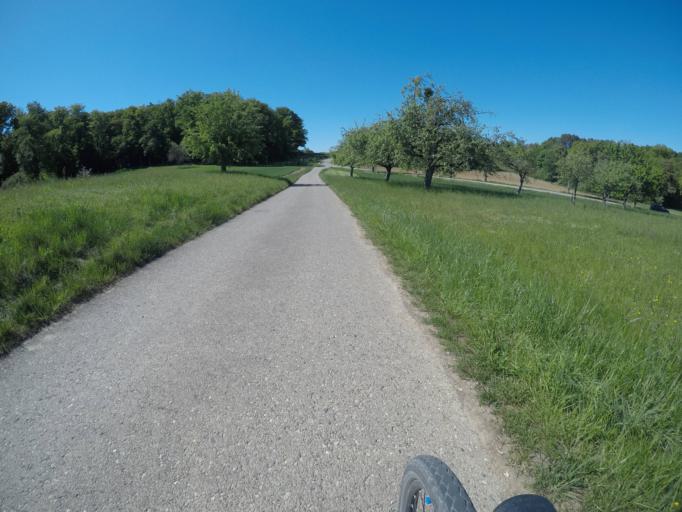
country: DE
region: Baden-Wuerttemberg
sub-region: Regierungsbezirk Stuttgart
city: Weissach
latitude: 48.8377
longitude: 8.8978
